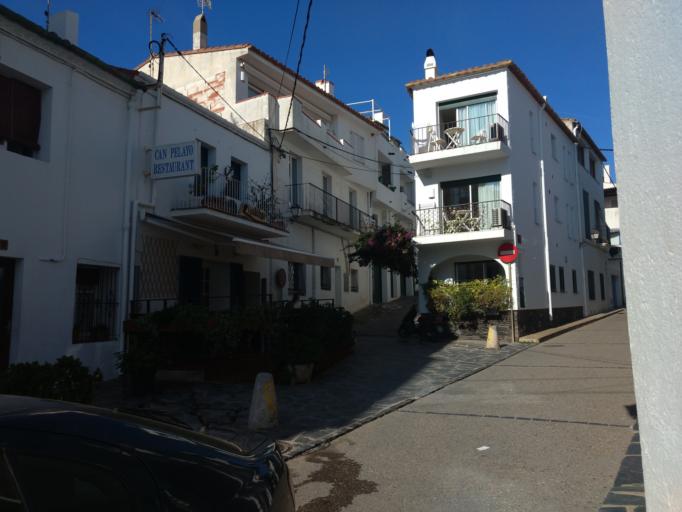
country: ES
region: Catalonia
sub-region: Provincia de Girona
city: Cadaques
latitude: 42.2874
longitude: 3.2751
